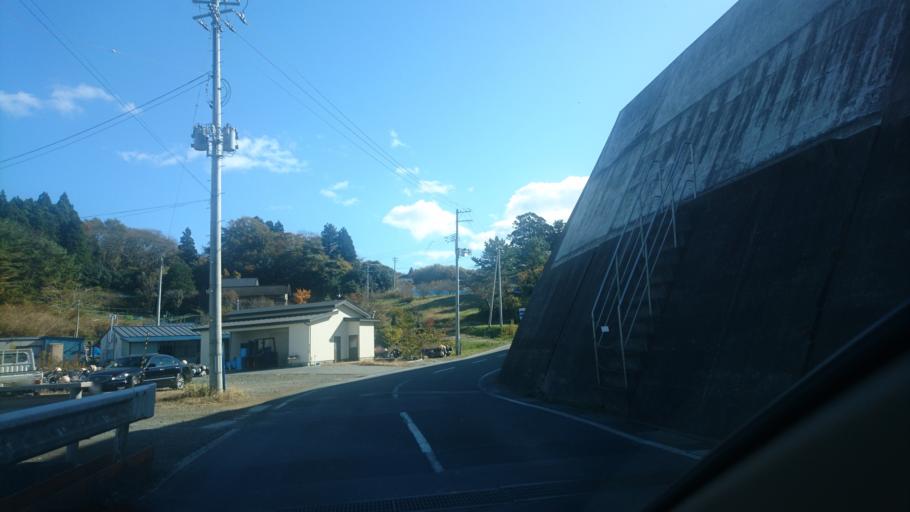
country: JP
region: Iwate
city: Ofunato
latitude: 38.9979
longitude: 141.7201
